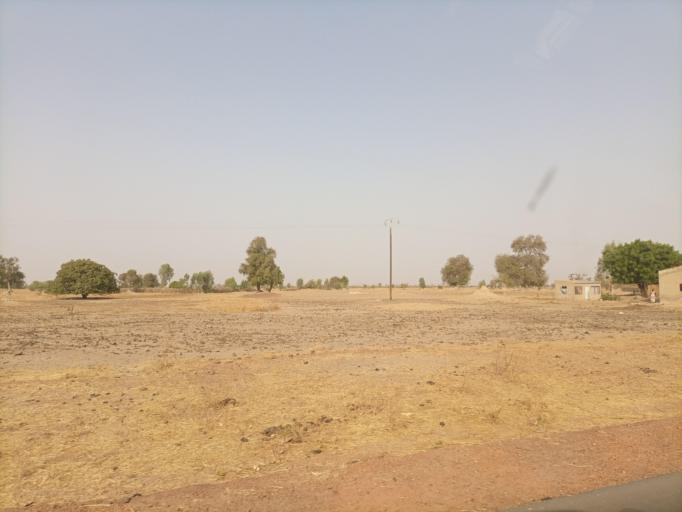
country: SN
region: Fatick
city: Passi
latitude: 14.0404
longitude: -16.3208
